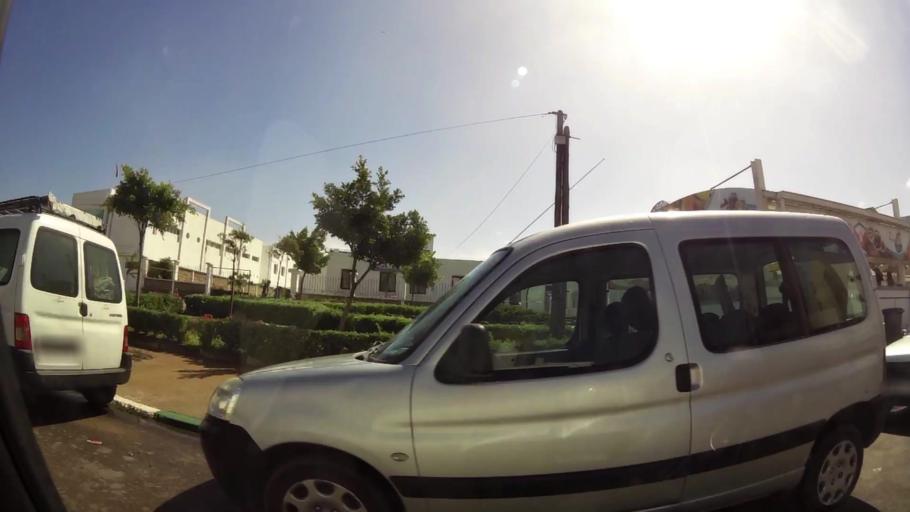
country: MA
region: Grand Casablanca
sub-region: Mediouna
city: Tit Mellil
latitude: 33.6203
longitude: -7.5063
